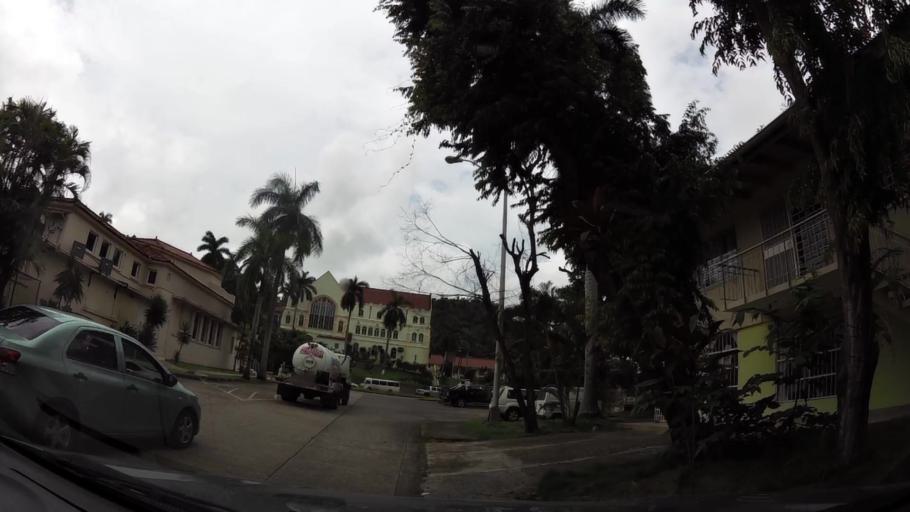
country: PA
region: Panama
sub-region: Distrito de Panama
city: Ancon
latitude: 8.9534
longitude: -79.5561
